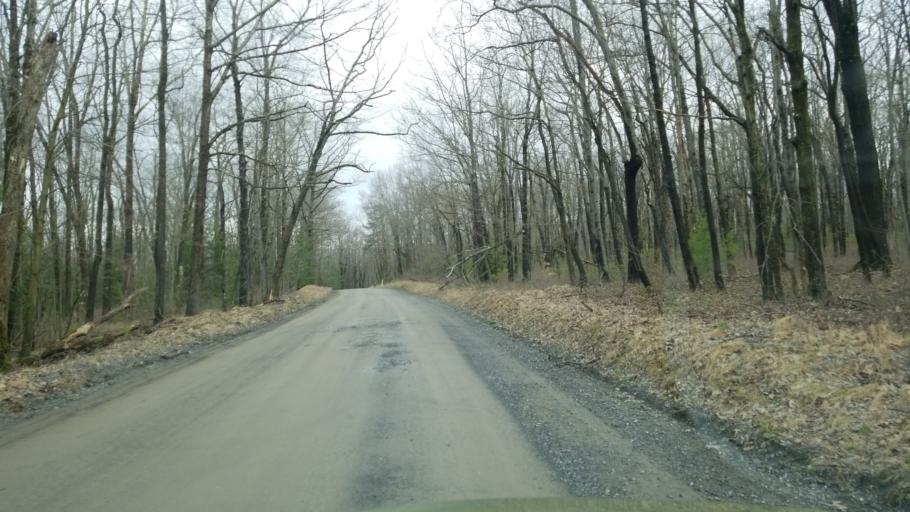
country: US
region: Pennsylvania
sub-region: Clearfield County
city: Shiloh
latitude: 41.1731
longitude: -78.3435
